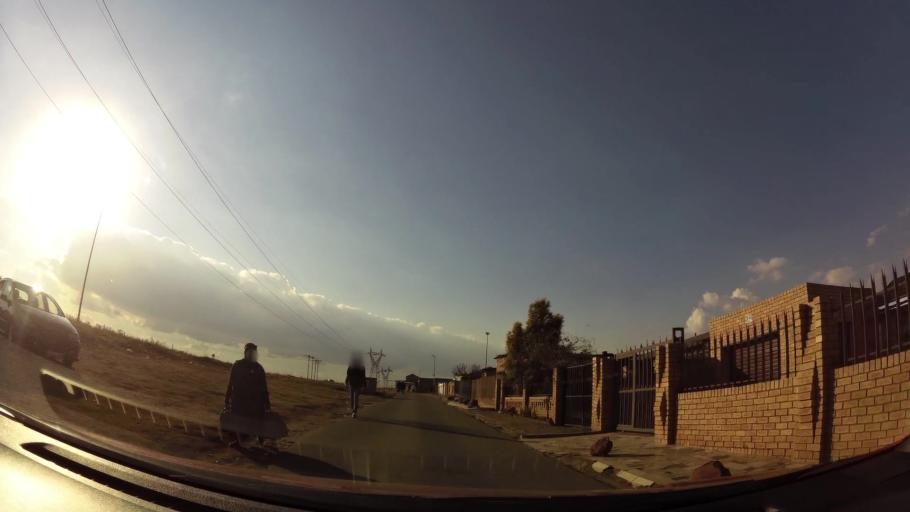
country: ZA
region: Gauteng
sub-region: City of Johannesburg Metropolitan Municipality
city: Soweto
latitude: -26.2326
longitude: 27.8588
